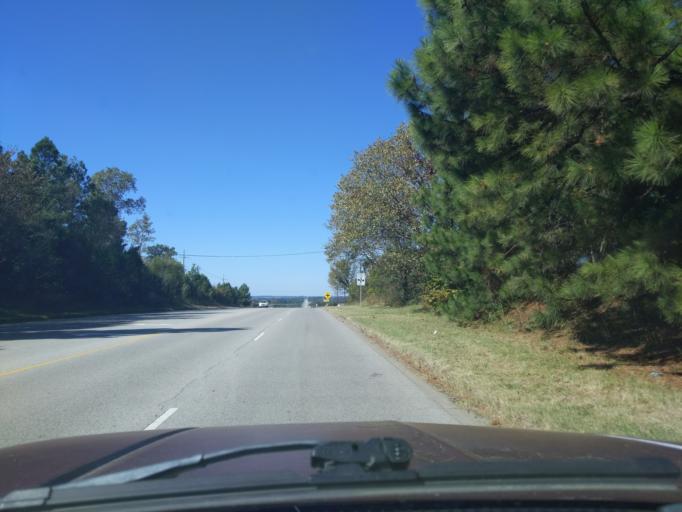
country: US
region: Oklahoma
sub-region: Tulsa County
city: Glenpool
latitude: 35.9884
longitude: -96.0442
